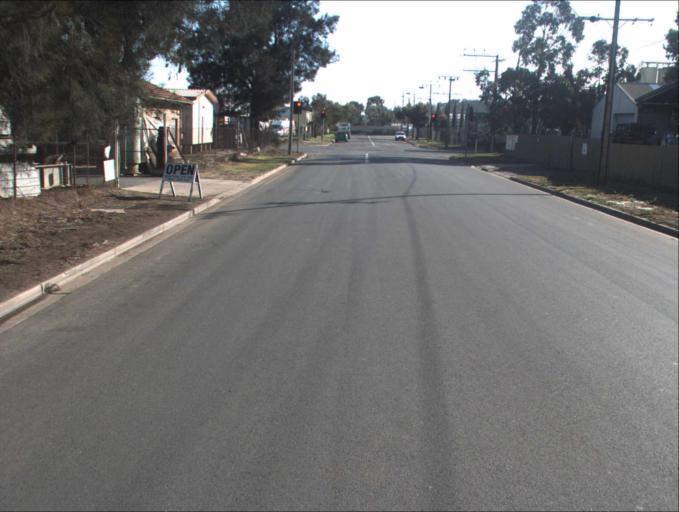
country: AU
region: South Australia
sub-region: Charles Sturt
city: Woodville North
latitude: -34.8419
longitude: 138.5507
